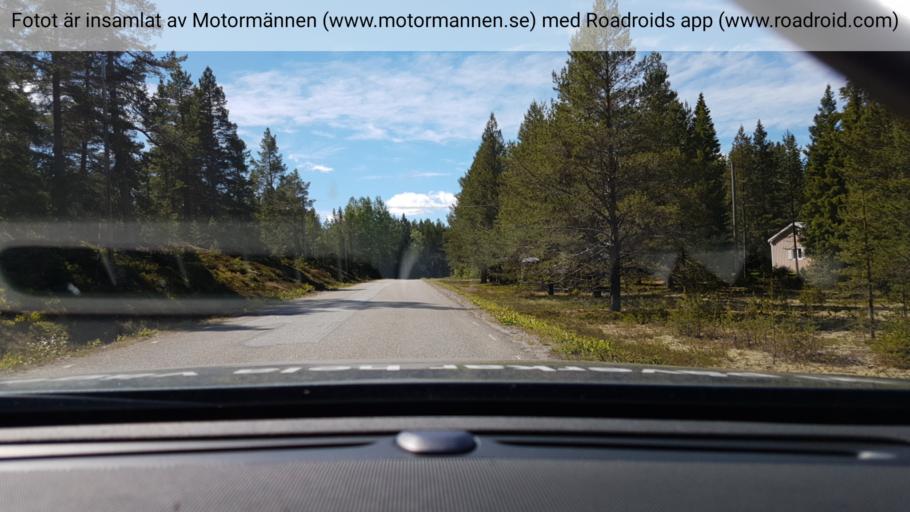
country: SE
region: Vaesterbotten
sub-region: Skelleftea Kommun
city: Burea
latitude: 64.4563
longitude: 21.5802
